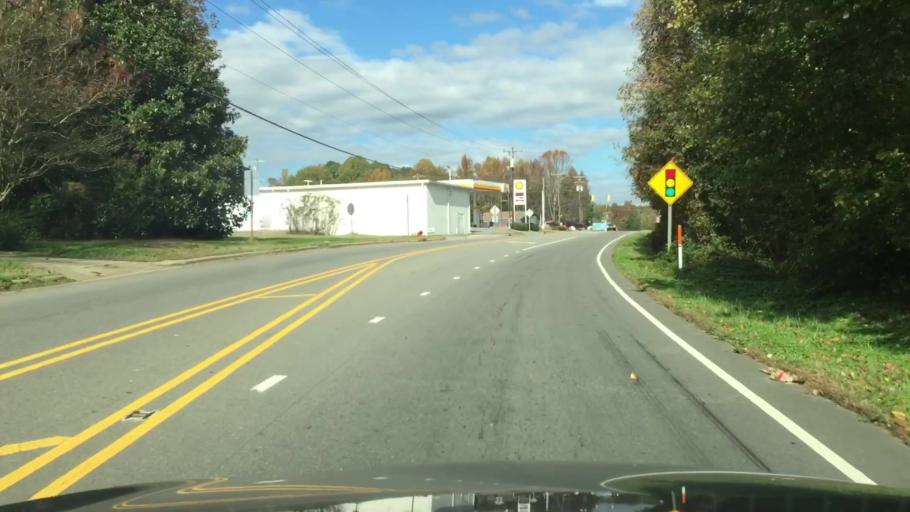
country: US
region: North Carolina
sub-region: Iredell County
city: Mooresville
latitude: 35.6218
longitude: -80.8261
